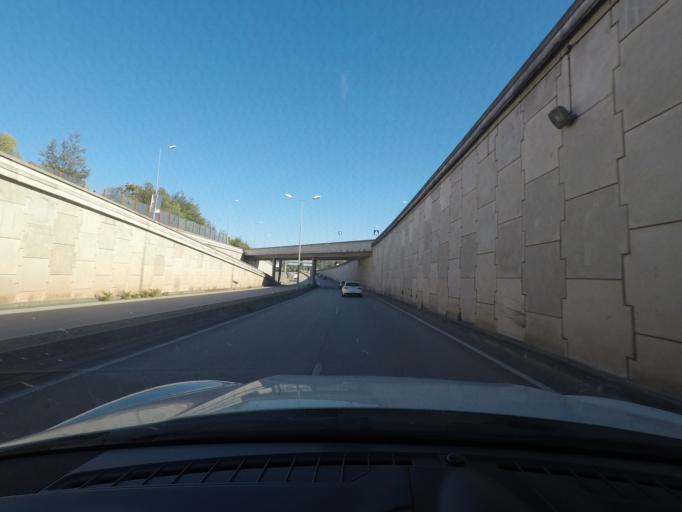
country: PT
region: Coimbra
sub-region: Coimbra
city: Coimbra
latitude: 40.1848
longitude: -8.4181
